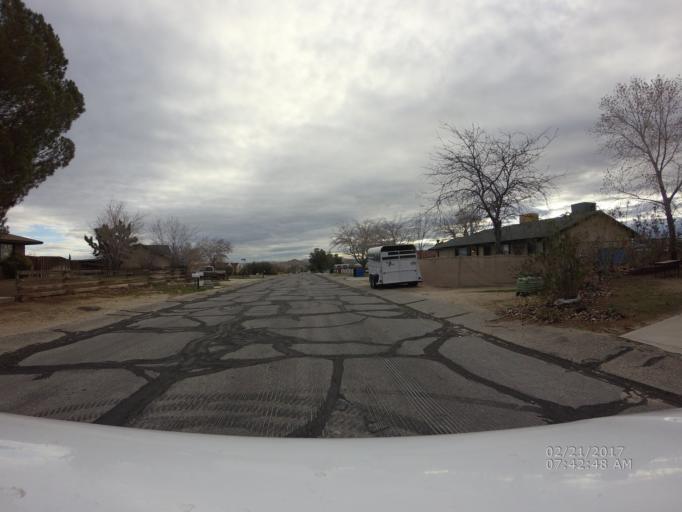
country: US
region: California
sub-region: Los Angeles County
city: Lake Los Angeles
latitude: 34.5936
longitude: -117.8408
